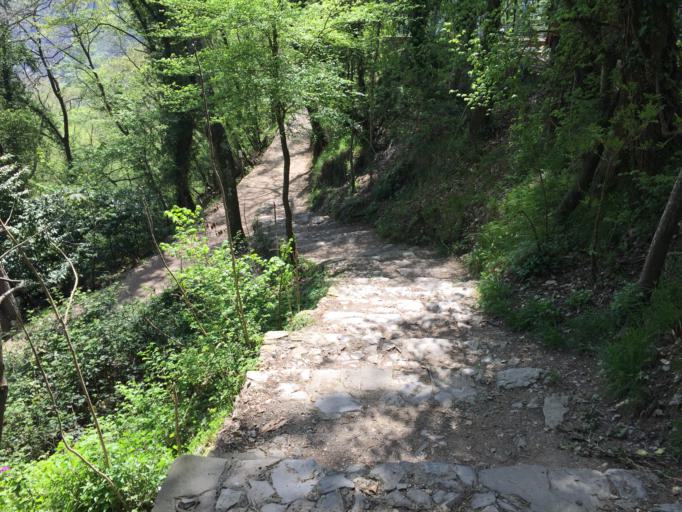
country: IT
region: Liguria
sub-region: Provincia di Genova
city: Camogli
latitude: 44.3326
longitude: 9.1713
